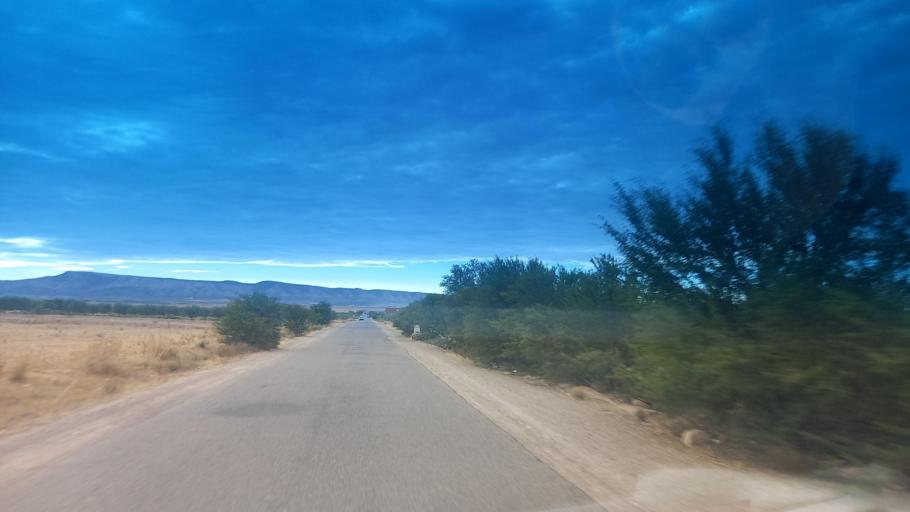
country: TN
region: Al Qasrayn
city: Sbiba
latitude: 35.3710
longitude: 9.0746
